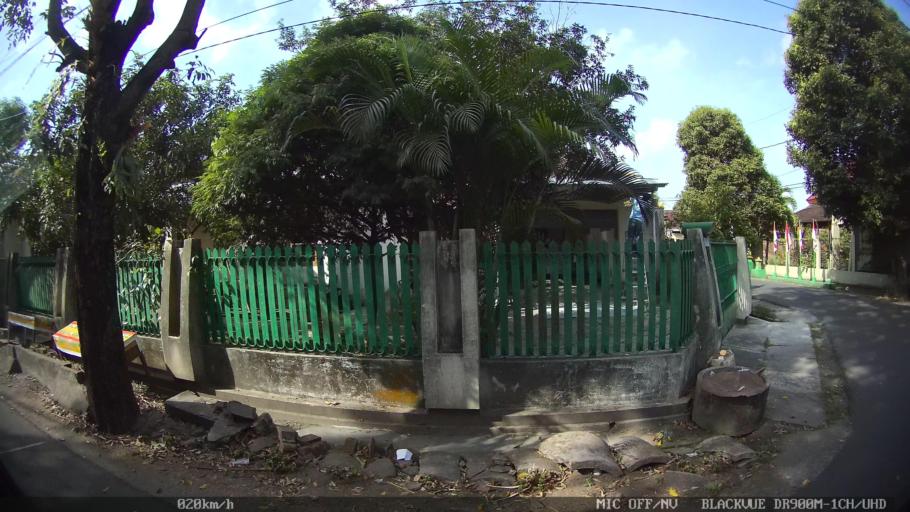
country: ID
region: Daerah Istimewa Yogyakarta
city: Kasihan
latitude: -7.8201
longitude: 110.3610
